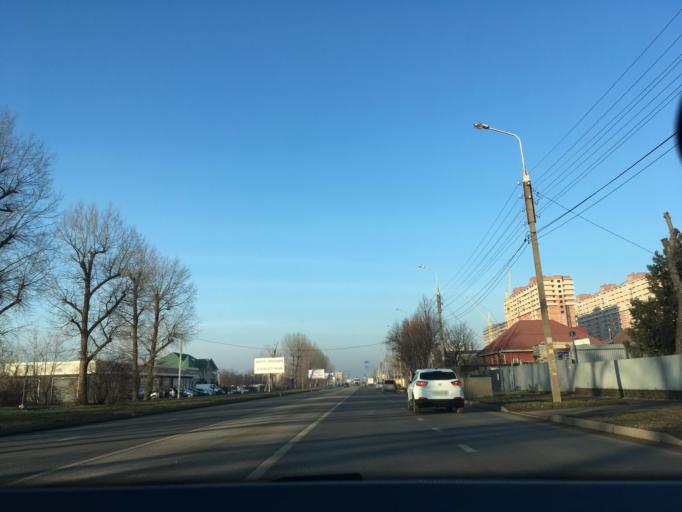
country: RU
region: Krasnodarskiy
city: Krasnodar
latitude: 45.1020
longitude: 39.0131
